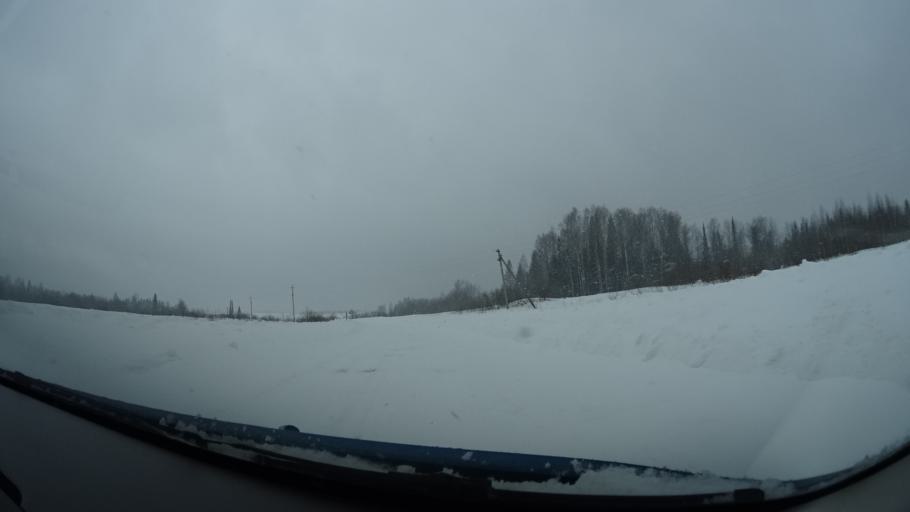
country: RU
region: Perm
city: Kuyeda
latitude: 56.6119
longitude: 55.7108
